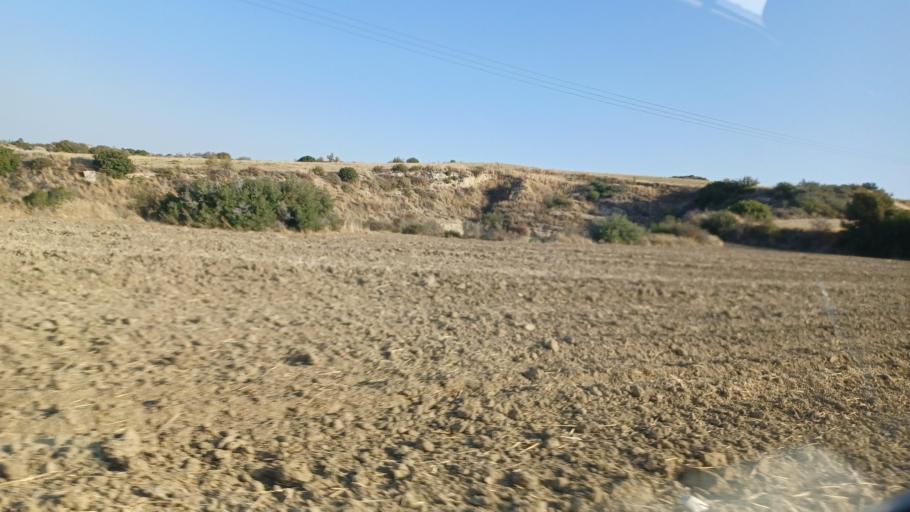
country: CY
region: Pafos
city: Polis
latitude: 34.9995
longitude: 32.4584
